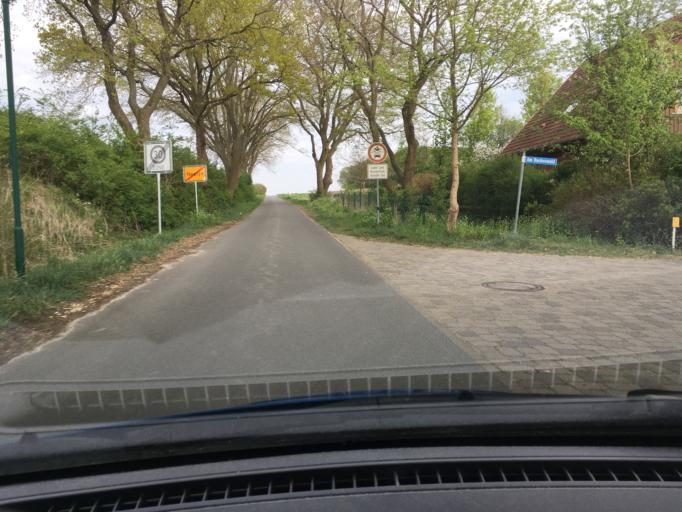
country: DE
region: Lower Saxony
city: Neetze
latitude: 53.2611
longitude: 10.6310
